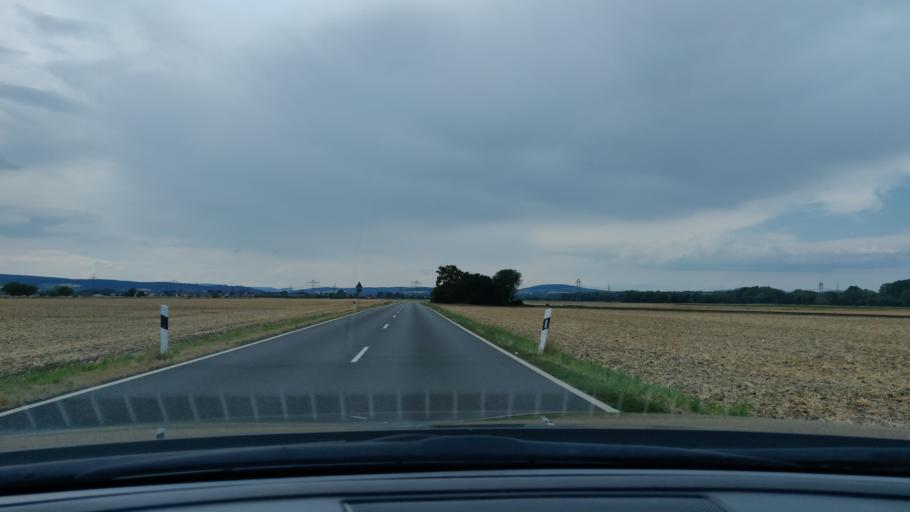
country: DE
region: Hesse
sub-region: Regierungsbezirk Kassel
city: Wabern
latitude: 51.1049
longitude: 9.3398
